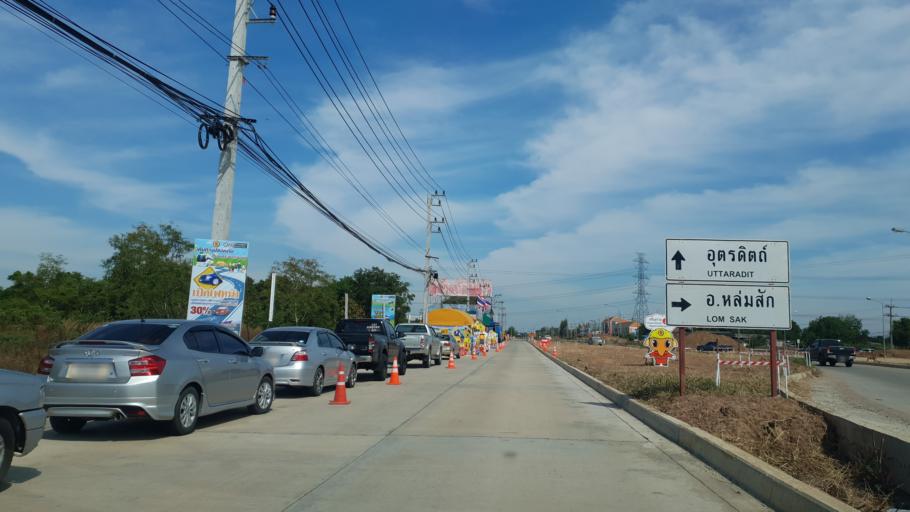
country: TH
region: Phitsanulok
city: Phitsanulok
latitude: 16.8190
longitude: 100.3300
